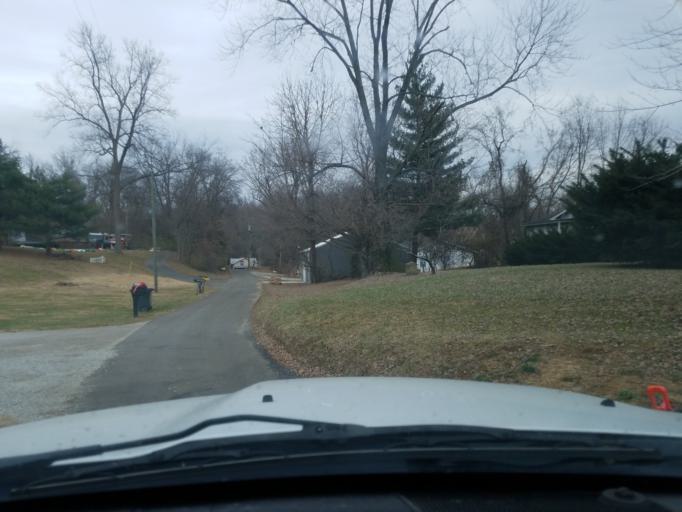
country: US
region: Kentucky
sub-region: Jefferson County
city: Prospect
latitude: 38.3369
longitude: -85.6544
